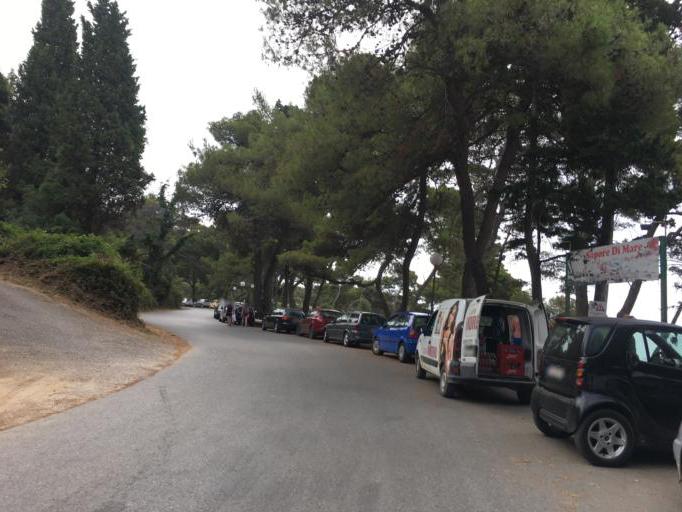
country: ME
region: Ulcinj
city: Ulcinj
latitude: 41.9206
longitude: 19.2118
